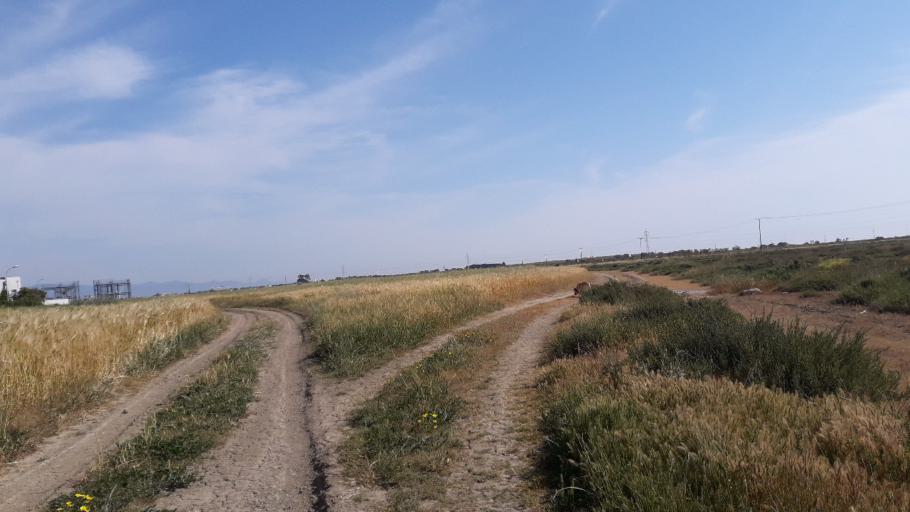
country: CY
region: Ammochostos
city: Famagusta
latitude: 35.1641
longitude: 33.8910
